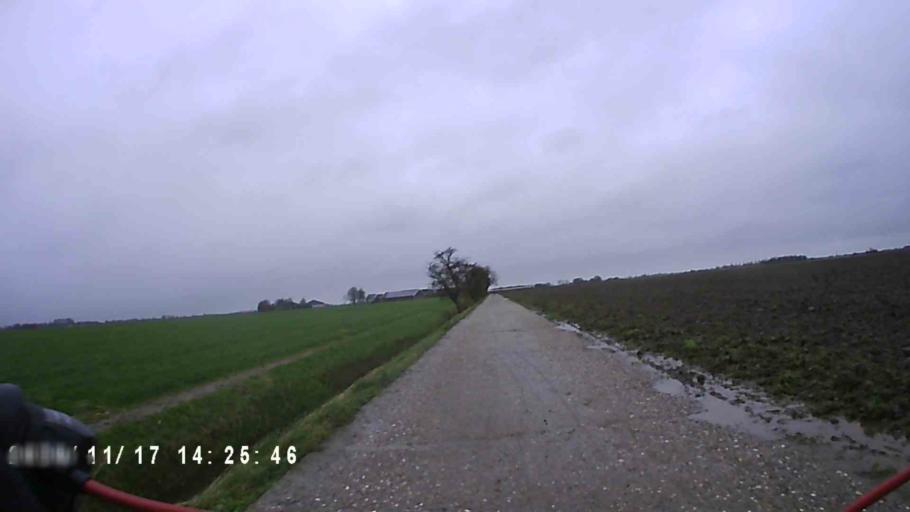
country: NL
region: Groningen
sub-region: Gemeente Zuidhorn
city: Grijpskerk
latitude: 53.2685
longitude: 6.3456
